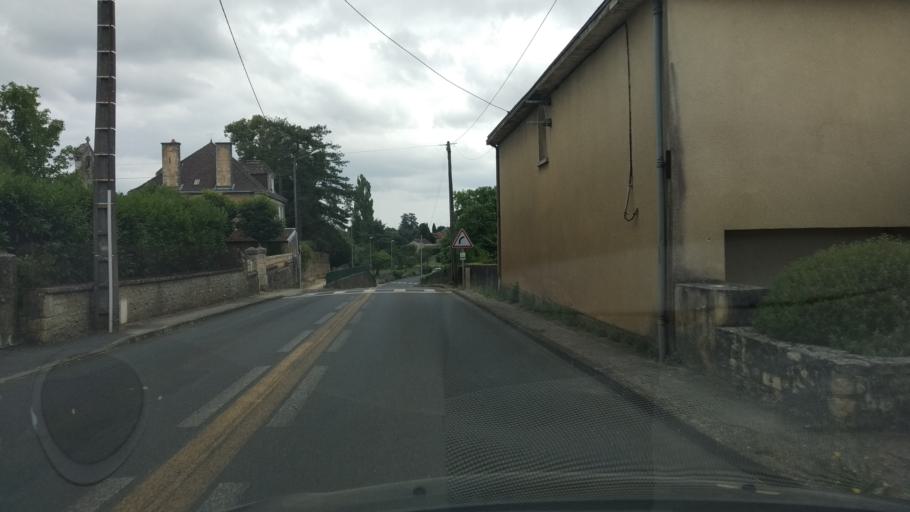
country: FR
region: Poitou-Charentes
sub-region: Departement de la Vienne
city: Roches-Premarie-Andille
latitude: 46.4834
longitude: 0.3700
